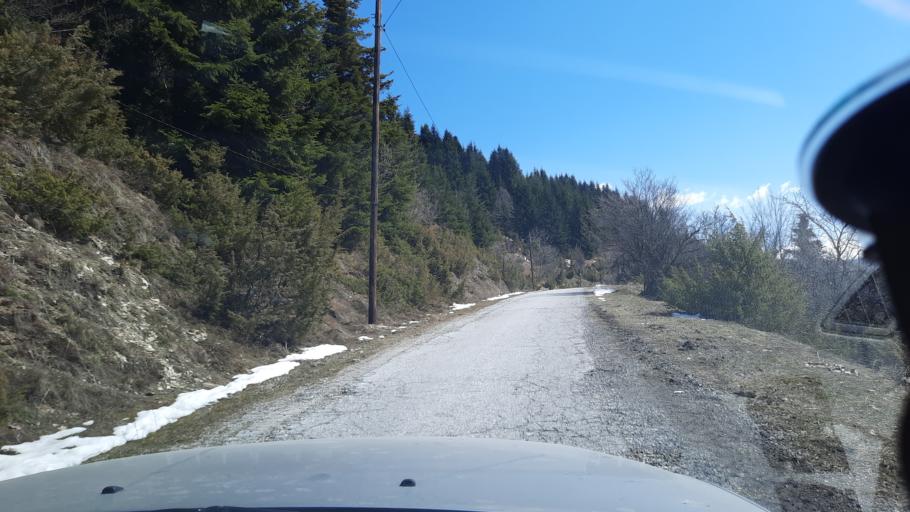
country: MK
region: Gostivar
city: Vrutok
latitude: 41.7130
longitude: 20.7299
